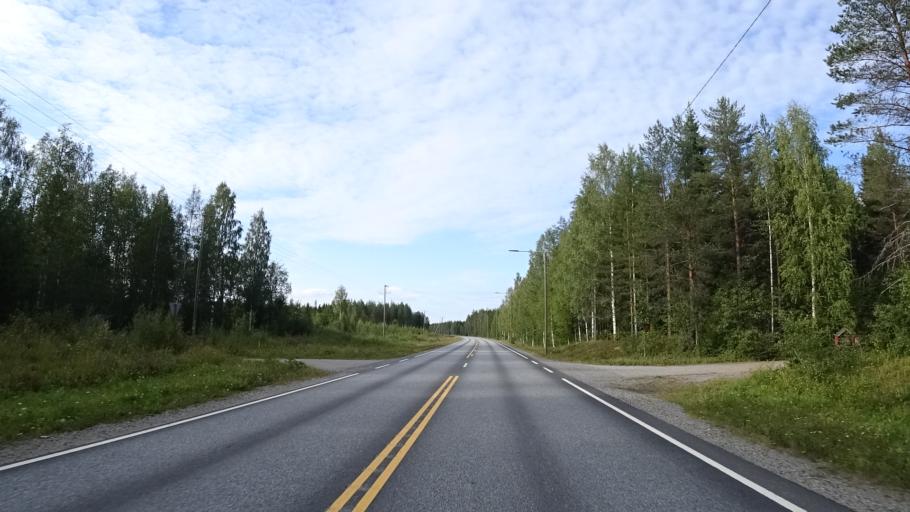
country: FI
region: North Karelia
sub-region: Joensuu
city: Eno
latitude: 62.8672
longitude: 30.2010
